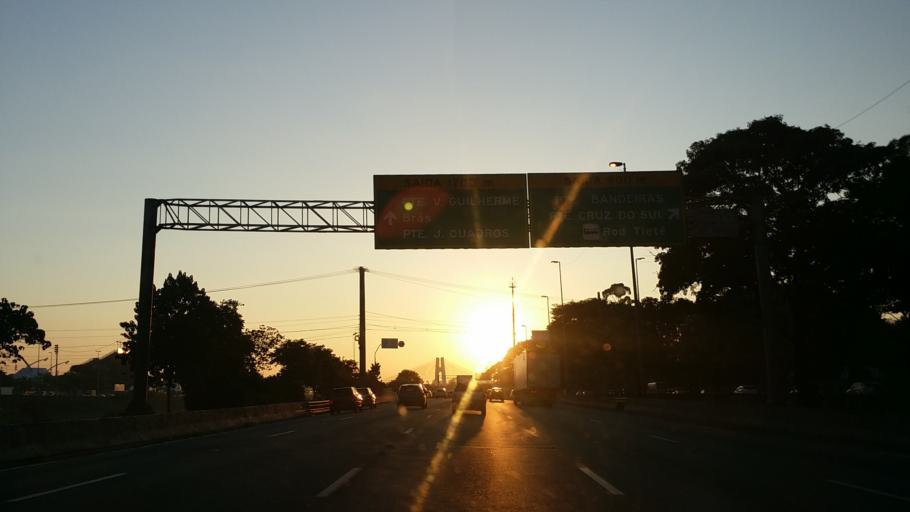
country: BR
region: Sao Paulo
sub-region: Sao Paulo
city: Sao Paulo
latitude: -23.5178
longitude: -46.6502
